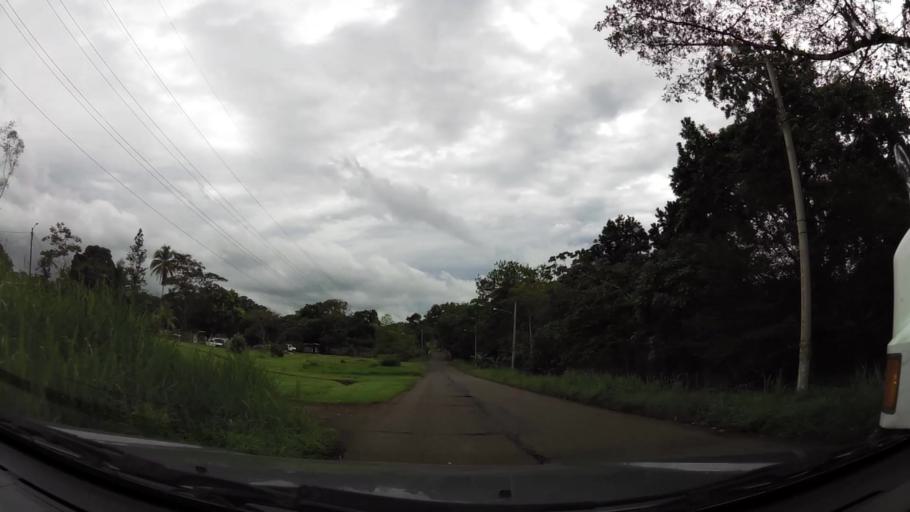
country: PA
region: Panama
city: Chilibre
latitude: 9.1550
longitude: -79.6180
